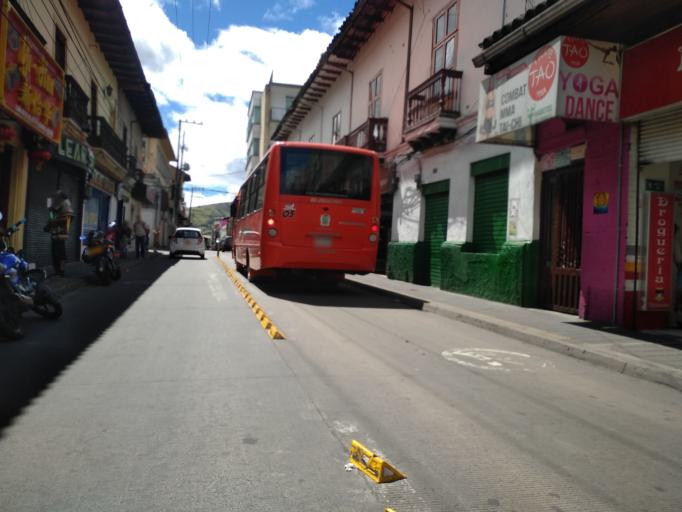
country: CO
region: Narino
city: Pasto
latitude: 1.2138
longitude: -77.2805
